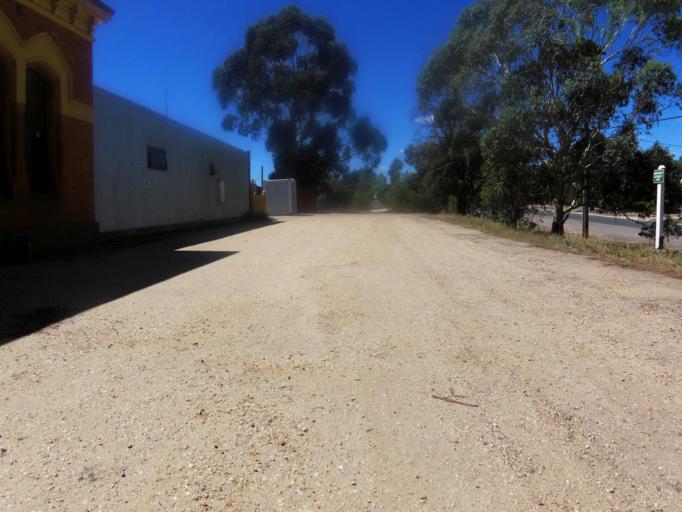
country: AU
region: Victoria
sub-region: Mount Alexander
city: Castlemaine
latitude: -36.9926
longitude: 144.0739
